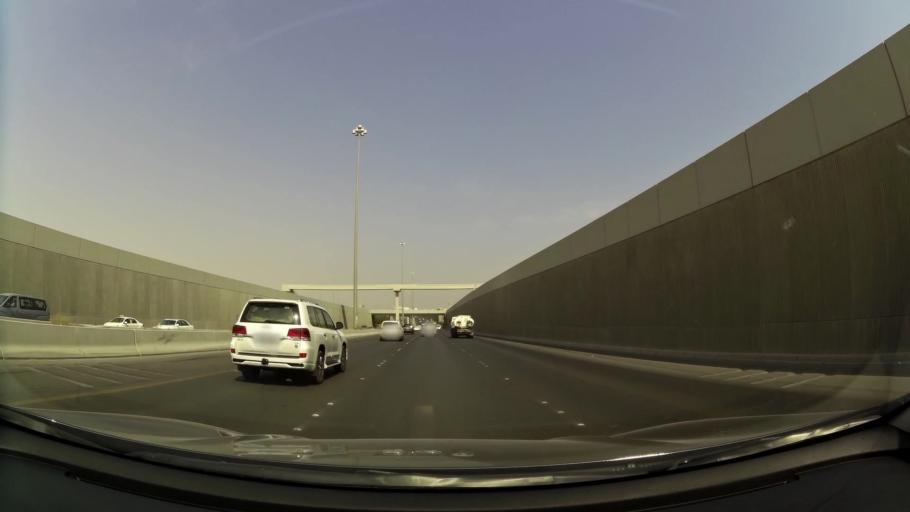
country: KW
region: Al Ahmadi
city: Al Manqaf
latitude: 29.1040
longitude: 48.1179
